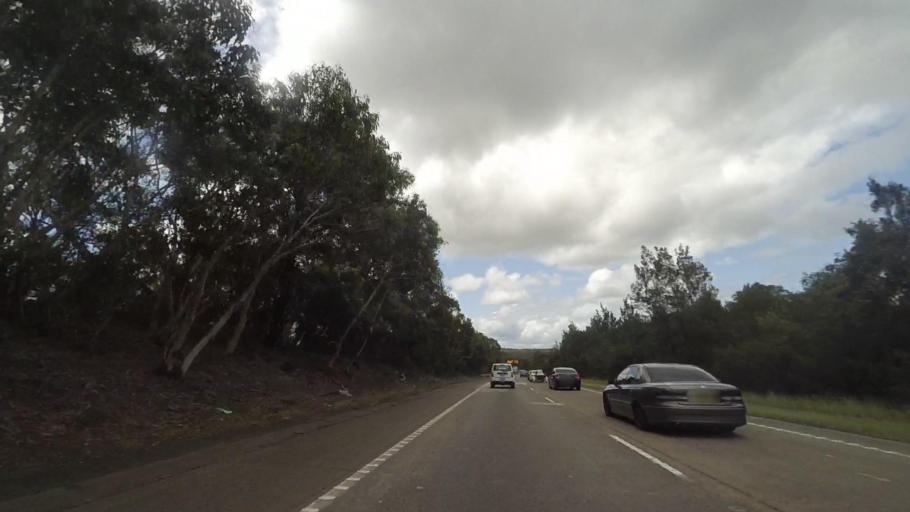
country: AU
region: New South Wales
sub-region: Gosford Shire
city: Narara
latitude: -33.3929
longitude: 151.2973
